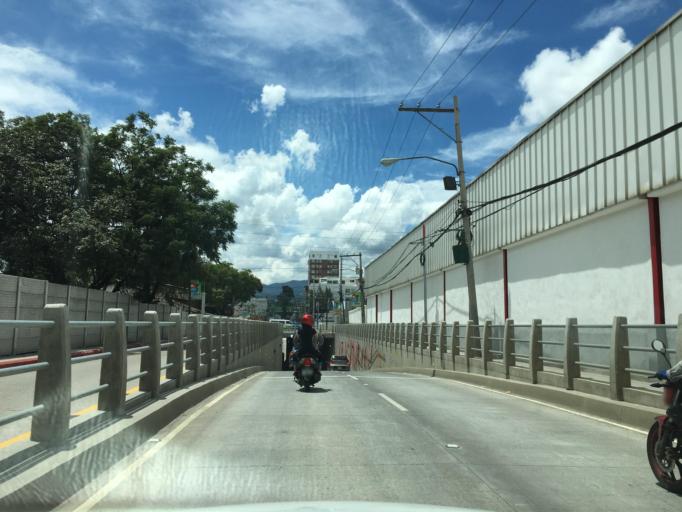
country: GT
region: Guatemala
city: Santa Catarina Pinula
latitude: 14.5891
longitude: -90.5408
